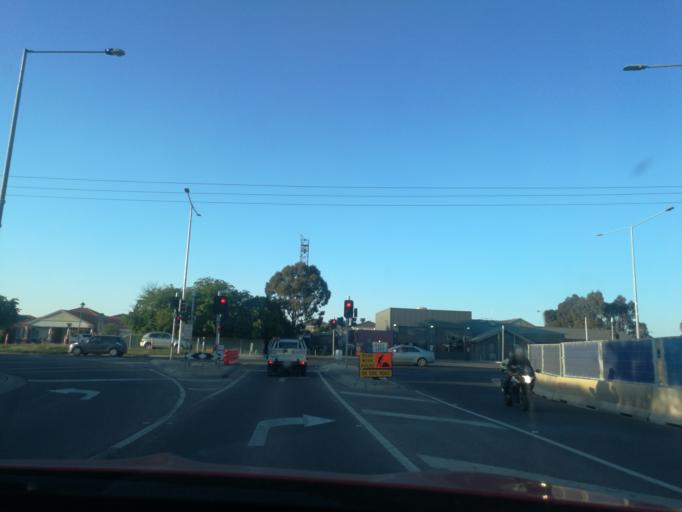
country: AU
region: Victoria
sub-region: Wyndham
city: Williams Landing
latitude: -37.8858
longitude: 144.7471
